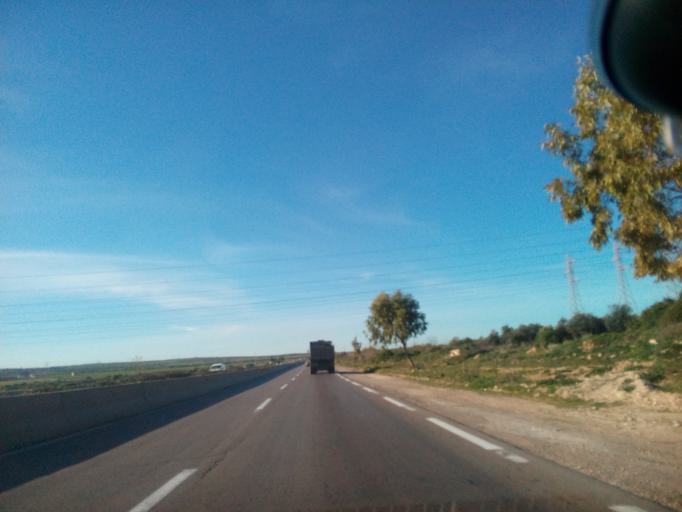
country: DZ
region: Oran
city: Ain el Bya
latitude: 35.7732
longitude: -0.1969
